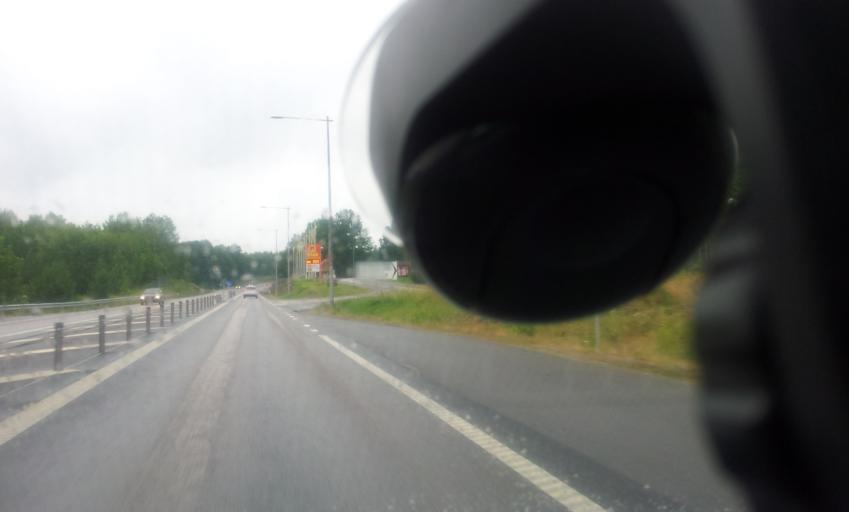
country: SE
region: Kalmar
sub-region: Vasterviks Kommun
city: Forserum
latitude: 57.9809
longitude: 16.4830
